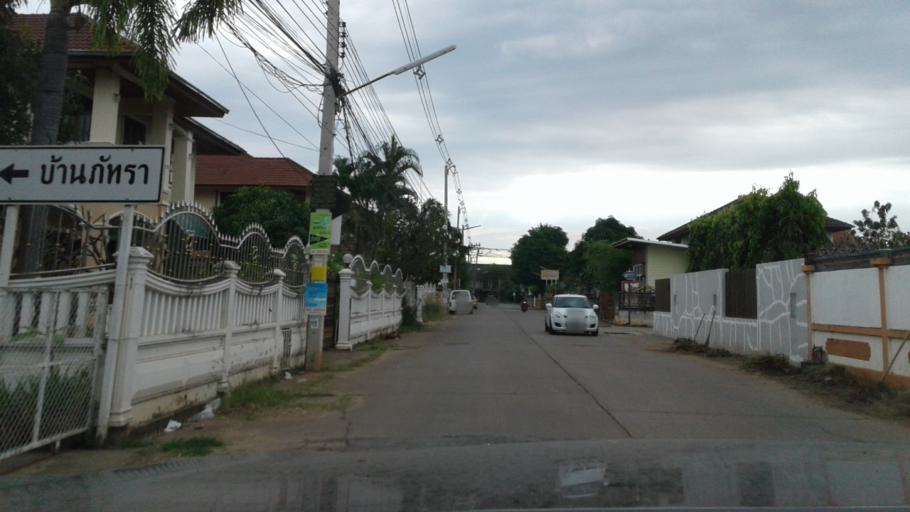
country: TH
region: Changwat Udon Thani
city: Udon Thani
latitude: 17.3992
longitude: 102.7750
